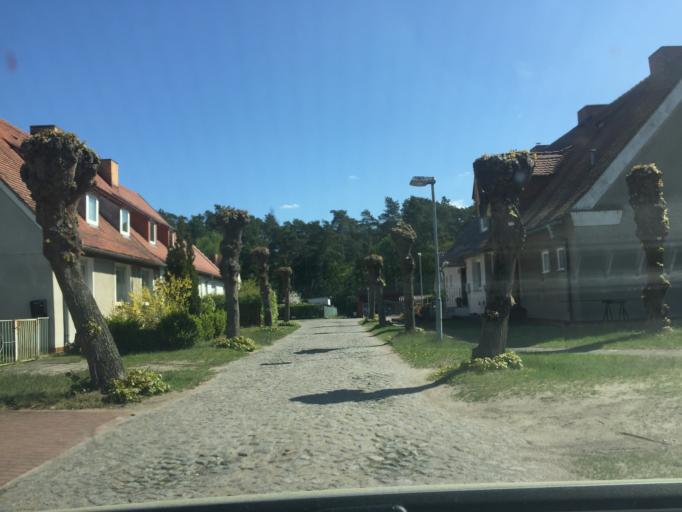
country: DE
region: Mecklenburg-Vorpommern
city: Torgelow
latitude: 53.6260
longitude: 14.0212
